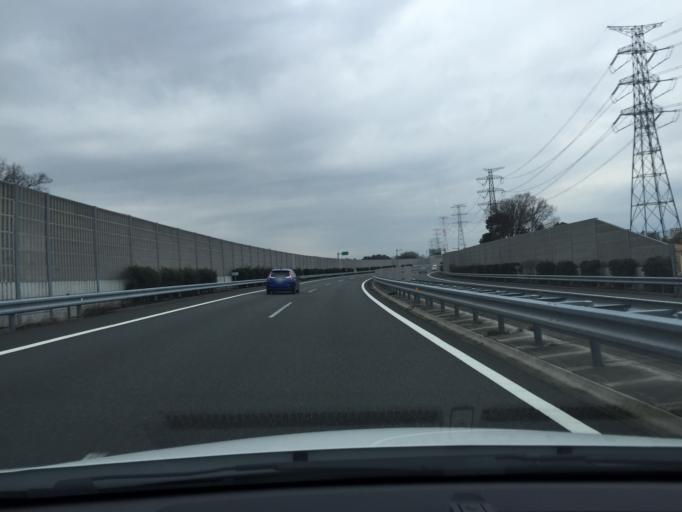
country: JP
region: Saitama
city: Sakado
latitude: 35.9515
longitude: 139.4260
